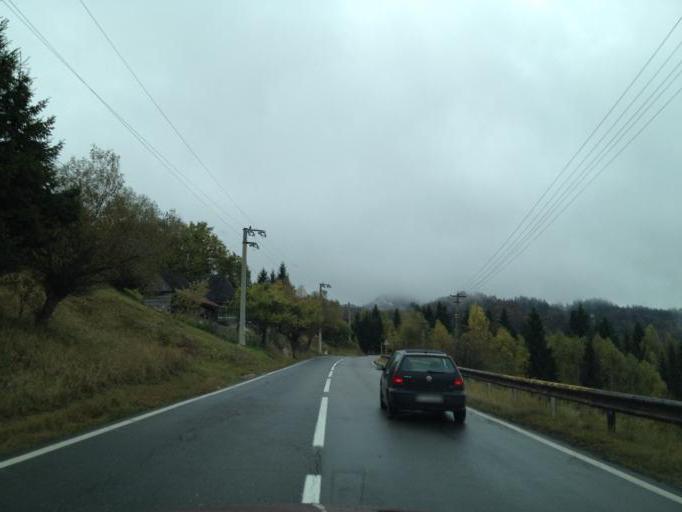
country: RO
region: Brasov
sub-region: Comuna Fundata
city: Fundata
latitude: 45.4665
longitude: 25.2933
